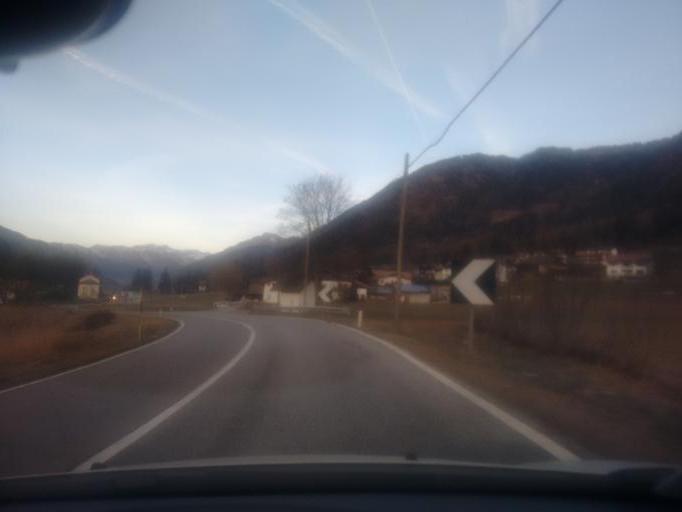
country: IT
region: Trentino-Alto Adige
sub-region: Bolzano
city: Campo di Trens
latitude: 46.8706
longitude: 11.4925
